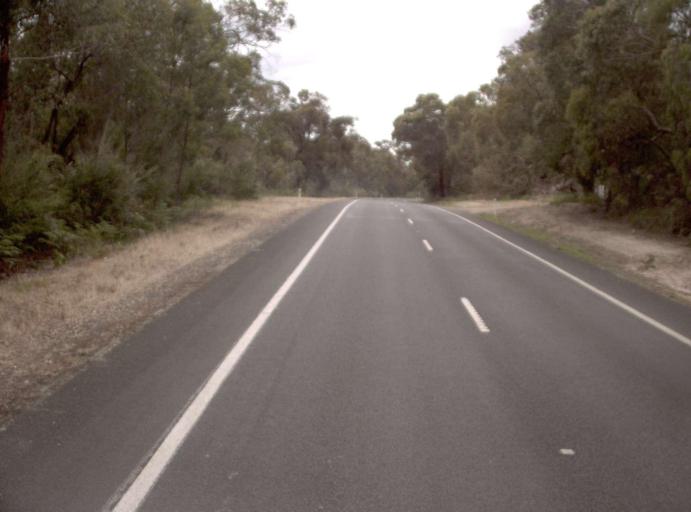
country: AU
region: Victoria
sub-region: Wellington
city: Sale
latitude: -38.2620
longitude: 147.0365
